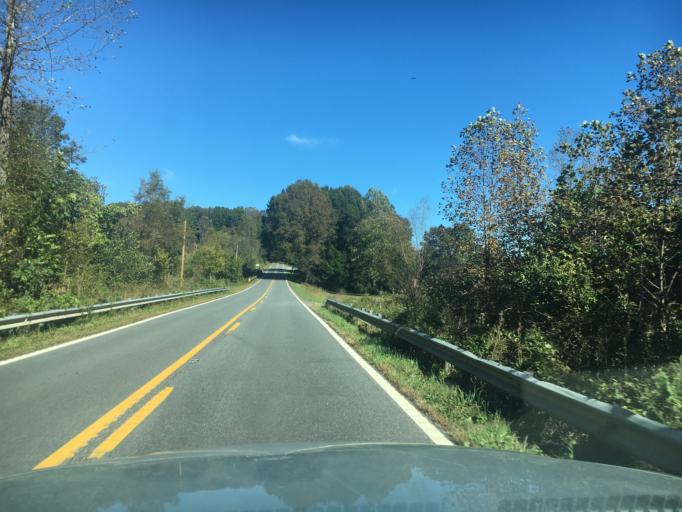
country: US
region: North Carolina
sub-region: Rutherford County
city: Spindale
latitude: 35.5050
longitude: -81.8566
